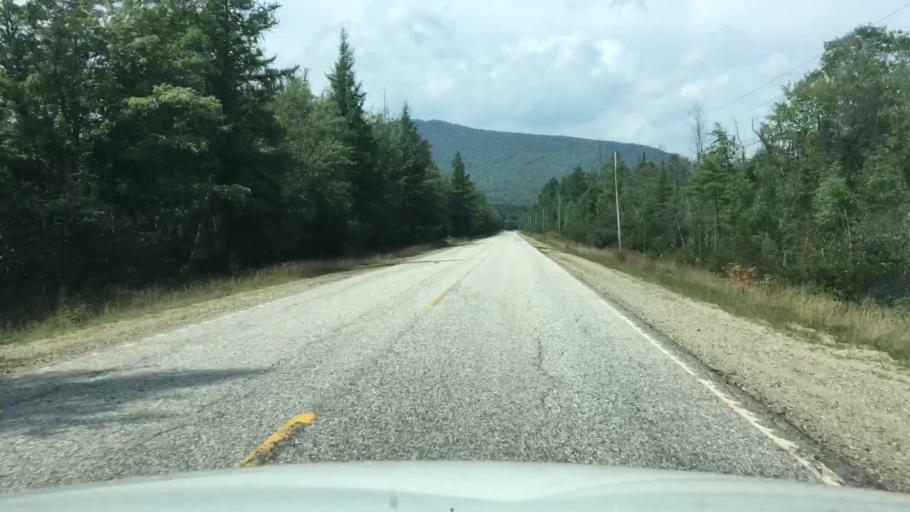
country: US
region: Maine
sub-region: Oxford County
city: Rumford
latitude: 44.5743
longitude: -70.7249
